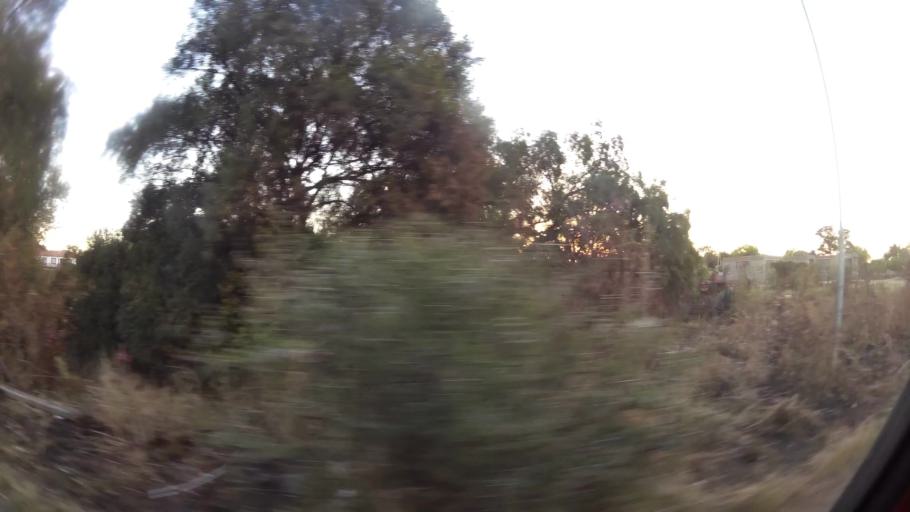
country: ZA
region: North-West
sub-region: Bojanala Platinum District Municipality
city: Rustenburg
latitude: -25.6194
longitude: 27.1951
